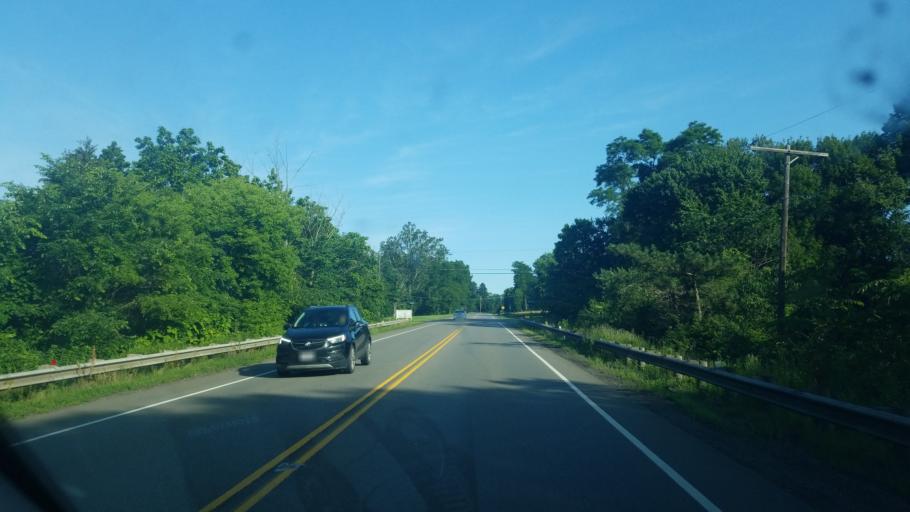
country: US
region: Ohio
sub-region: Columbiana County
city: Columbiana
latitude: 40.9070
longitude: -80.7037
